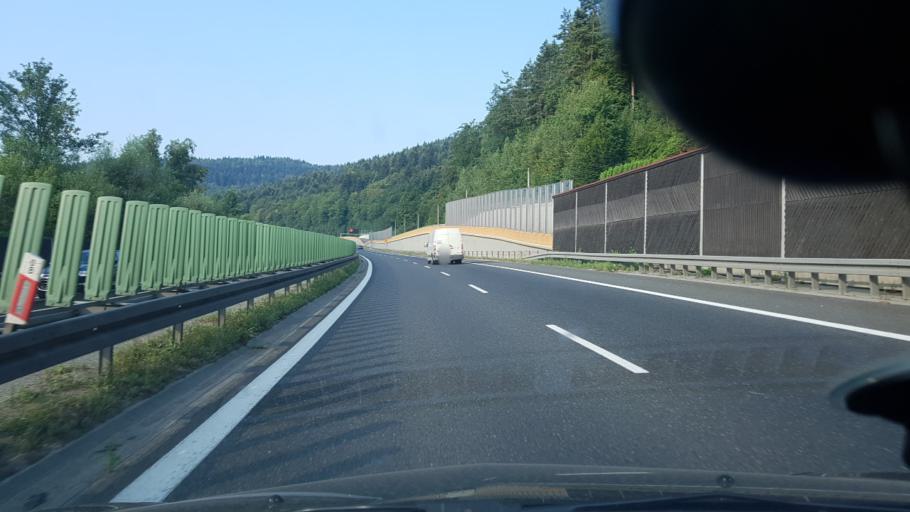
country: PL
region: Lesser Poland Voivodeship
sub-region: Powiat myslenicki
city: Myslenice
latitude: 49.8168
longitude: 19.9280
